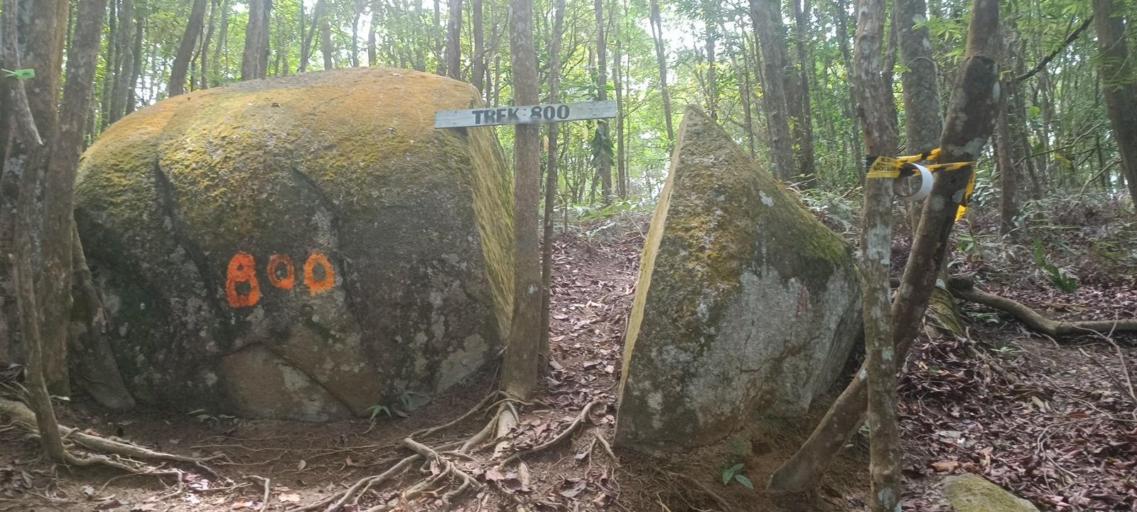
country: MY
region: Penang
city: Bukit Mertajam
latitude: 5.3672
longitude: 100.4977
